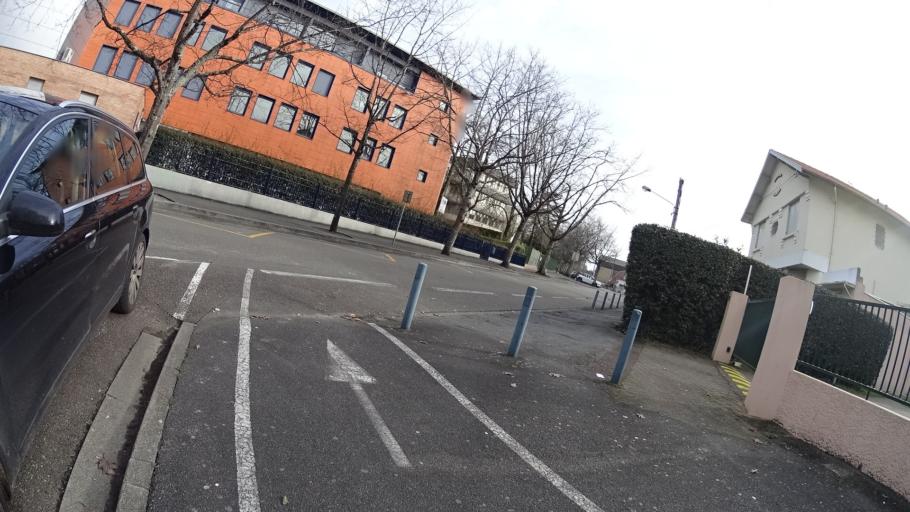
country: FR
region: Aquitaine
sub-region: Departement des Landes
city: Dax
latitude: 43.7019
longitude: -1.0566
